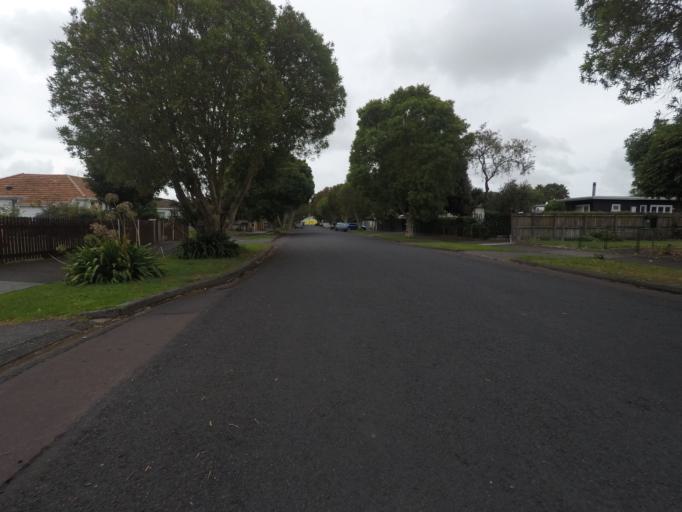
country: NZ
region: Auckland
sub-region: Auckland
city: Rosebank
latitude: -36.8895
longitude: 174.6837
